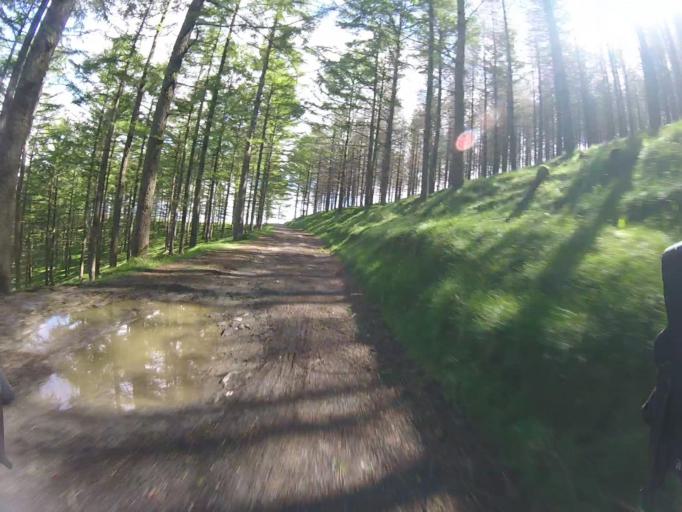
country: ES
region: Navarre
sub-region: Provincia de Navarra
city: Arano
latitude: 43.1750
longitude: -1.9222
